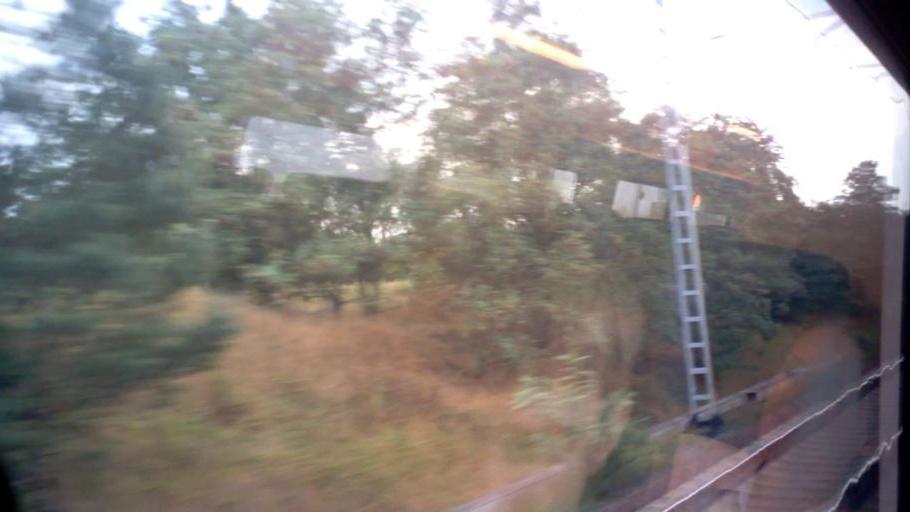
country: DE
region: Berlin
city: Lichtenrade
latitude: 52.3578
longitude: 13.4376
